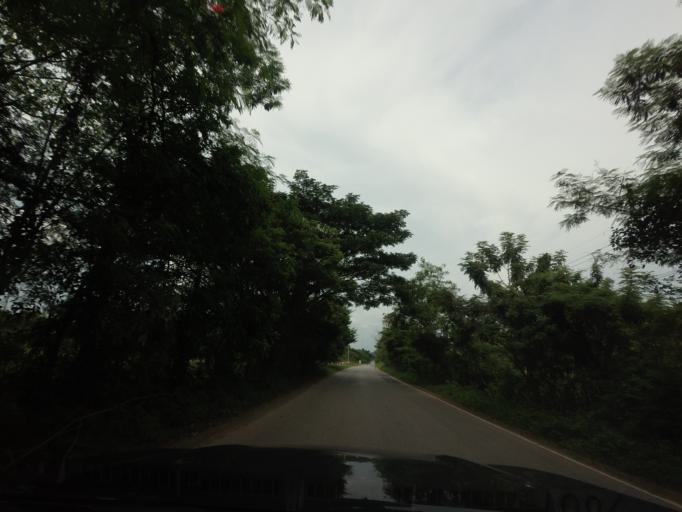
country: TH
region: Changwat Nong Bua Lamphu
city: Suwannakhuha
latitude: 17.4728
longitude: 102.3537
